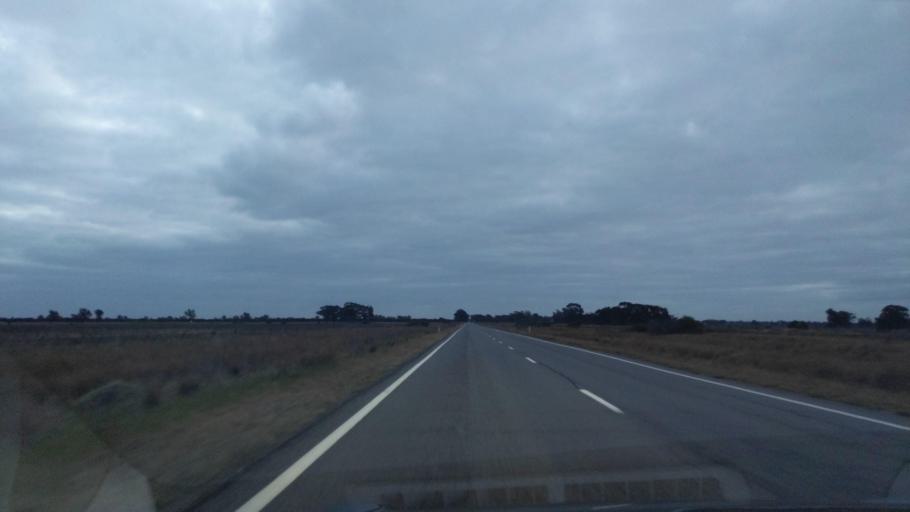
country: AU
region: New South Wales
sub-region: Coolamon
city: Coolamon
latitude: -34.7593
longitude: 146.8784
